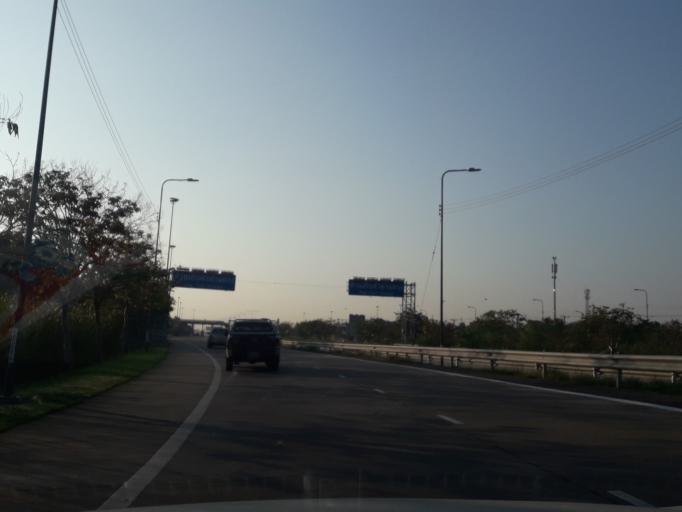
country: TH
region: Phra Nakhon Si Ayutthaya
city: Bang Pa-in
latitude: 14.1473
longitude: 100.5554
